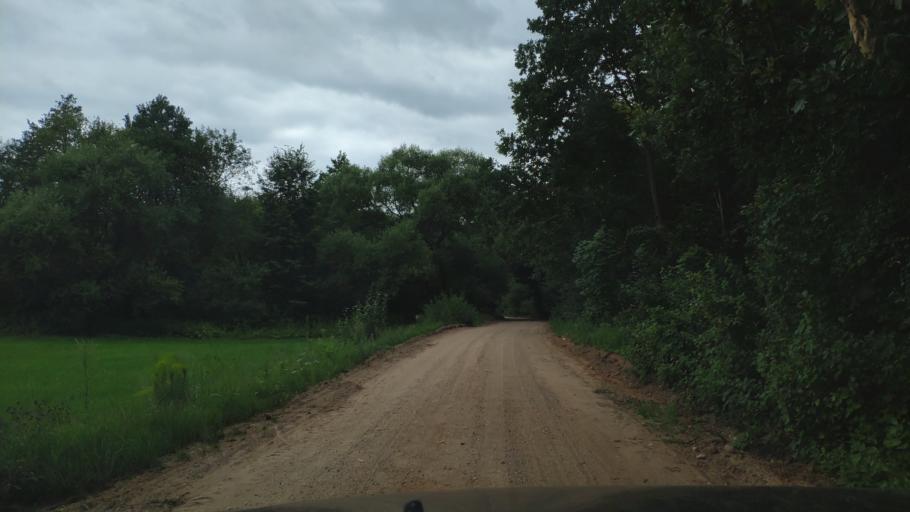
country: BY
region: Minsk
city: Khatsyezhyna
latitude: 53.9353
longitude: 27.2719
